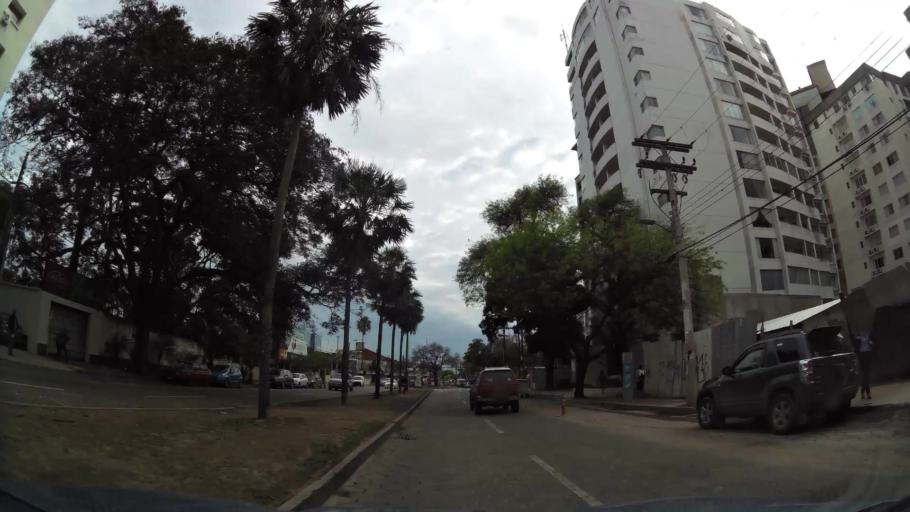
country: BO
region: Santa Cruz
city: Santa Cruz de la Sierra
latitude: -17.7912
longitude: -63.1779
